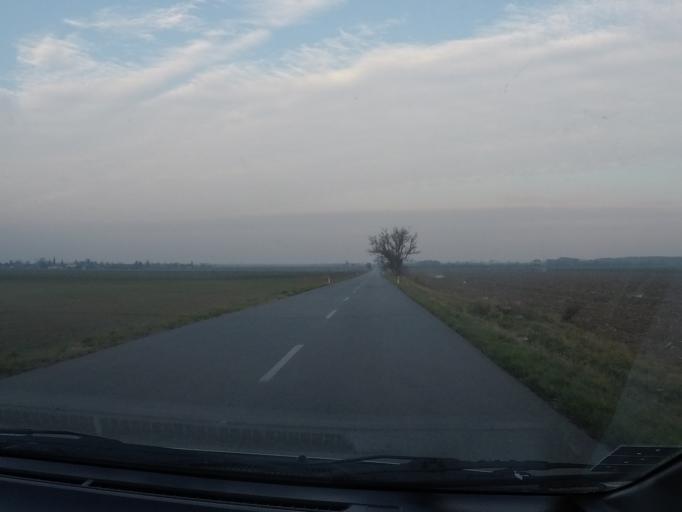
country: SK
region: Nitriansky
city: Svodin
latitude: 48.0749
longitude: 18.4814
